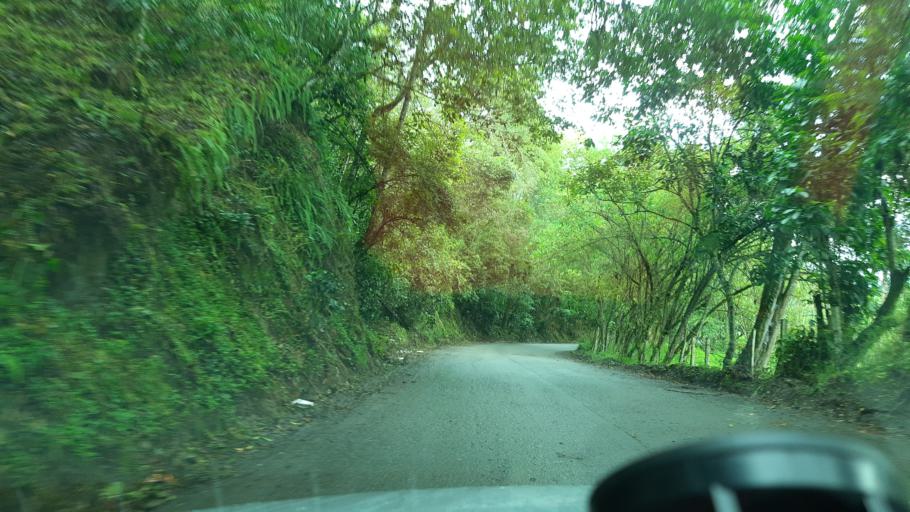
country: CO
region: Boyaca
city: Chinavita
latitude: 5.1359
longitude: -73.3622
